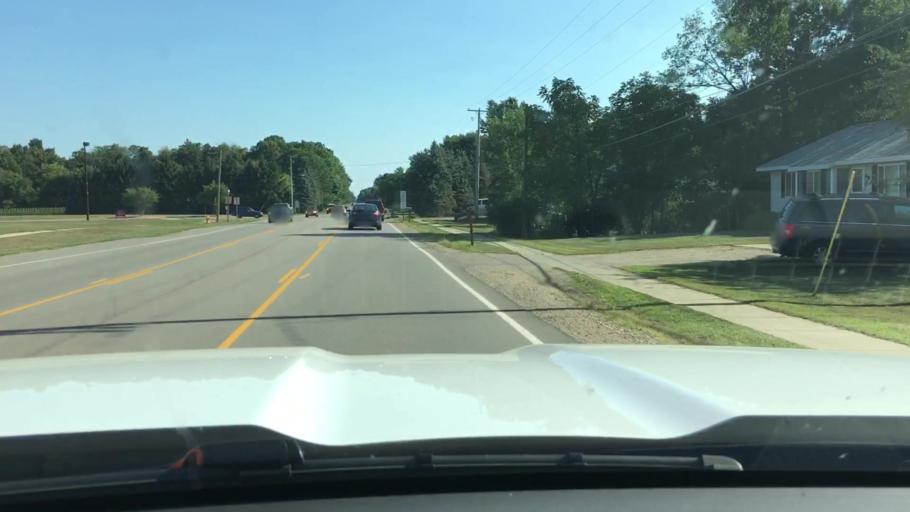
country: US
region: Michigan
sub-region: Ottawa County
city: Allendale
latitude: 42.9641
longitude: -85.9538
